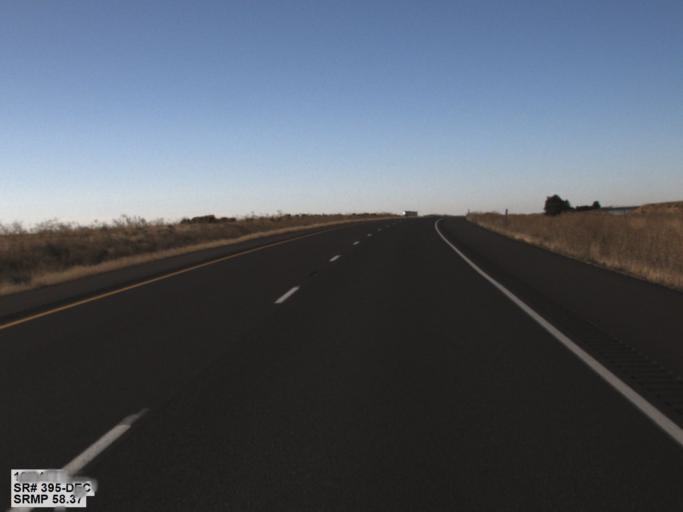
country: US
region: Washington
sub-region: Franklin County
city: Connell
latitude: 46.6974
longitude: -118.8367
